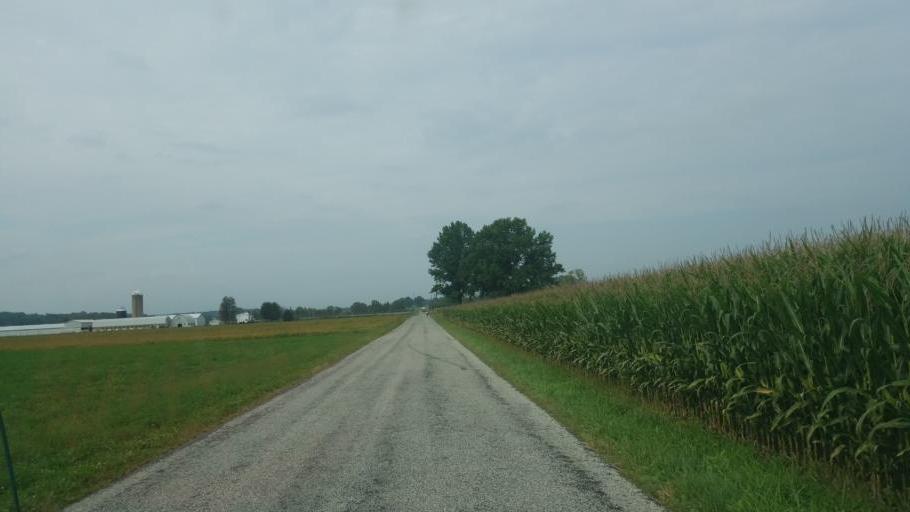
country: US
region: Ohio
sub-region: Wayne County
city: Rittman
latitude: 40.9571
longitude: -81.8122
